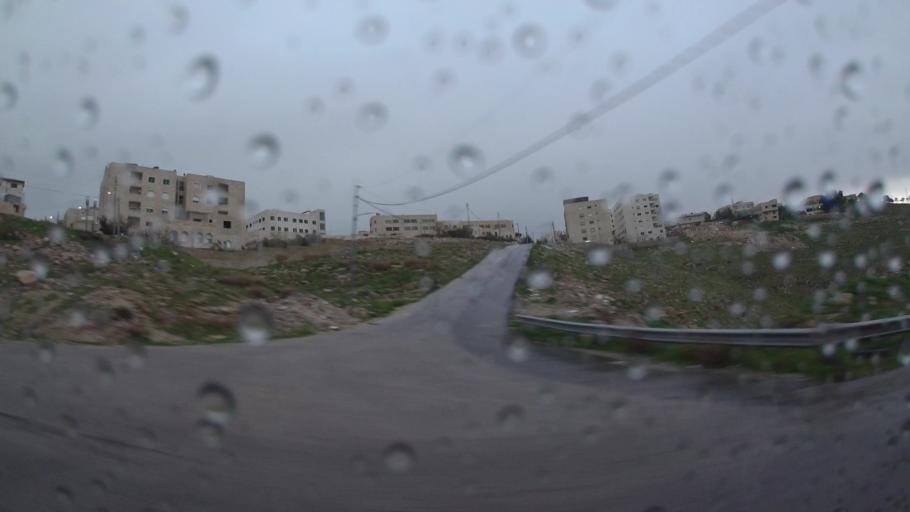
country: JO
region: Amman
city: Amman
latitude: 31.9983
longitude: 35.9690
